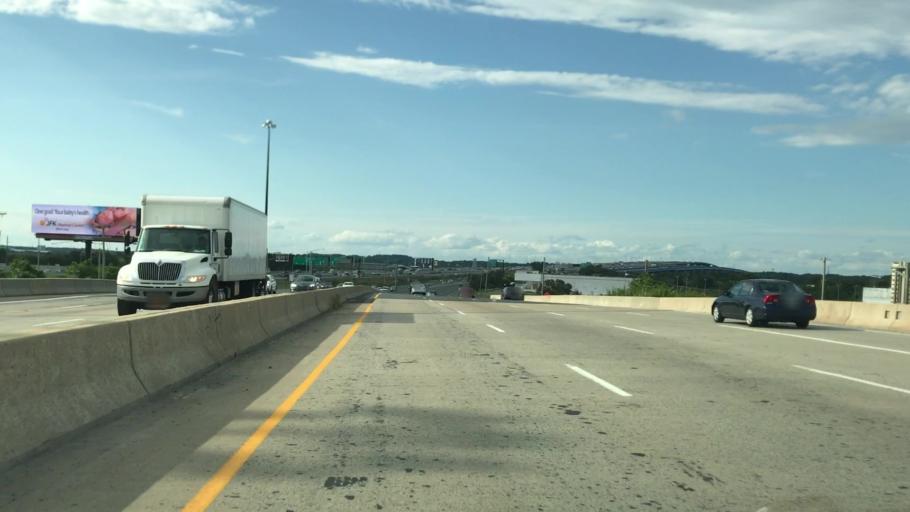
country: US
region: New Jersey
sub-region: Middlesex County
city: South Amboy
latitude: 40.4963
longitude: -74.2981
